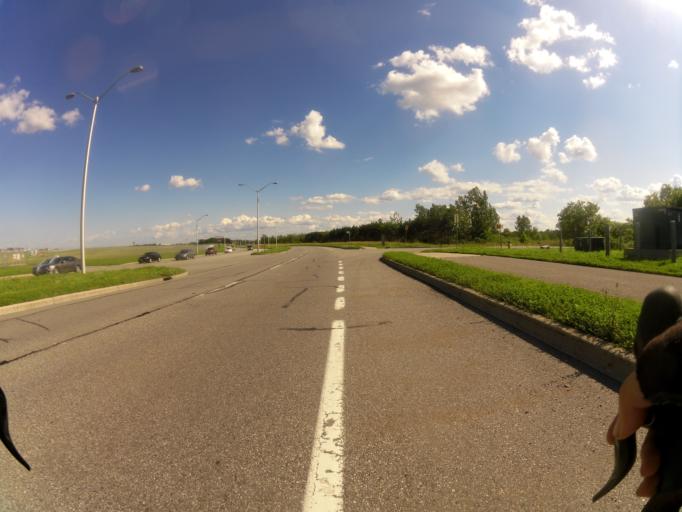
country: CA
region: Ontario
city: Ottawa
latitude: 45.3300
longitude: -75.6940
